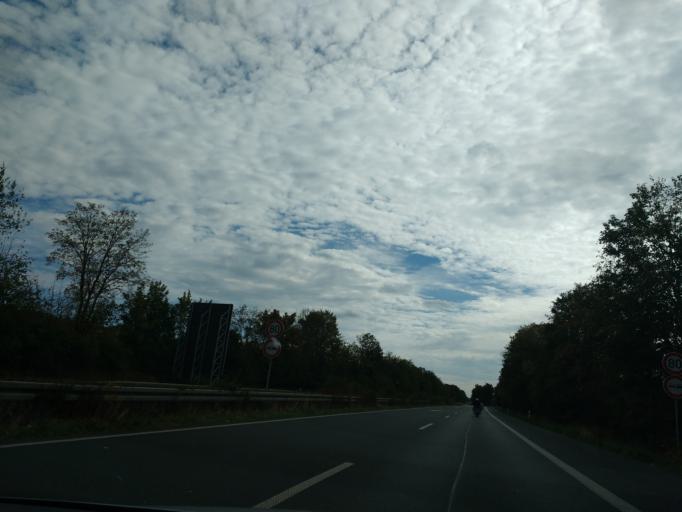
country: DE
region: North Rhine-Westphalia
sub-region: Regierungsbezirk Arnsberg
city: Anrochte
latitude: 51.5747
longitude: 8.3111
